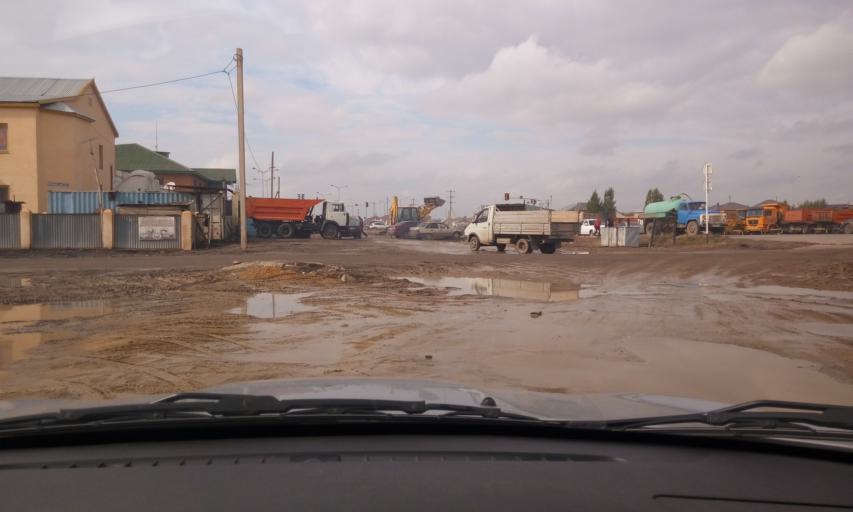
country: KZ
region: Astana Qalasy
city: Astana
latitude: 51.1363
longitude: 71.5230
